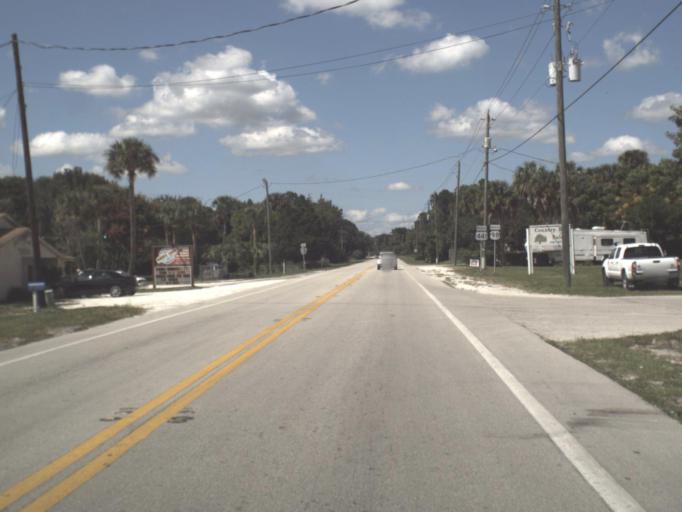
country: US
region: Florida
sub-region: Okeechobee County
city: Taylor Creek
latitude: 27.1827
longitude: -80.7368
